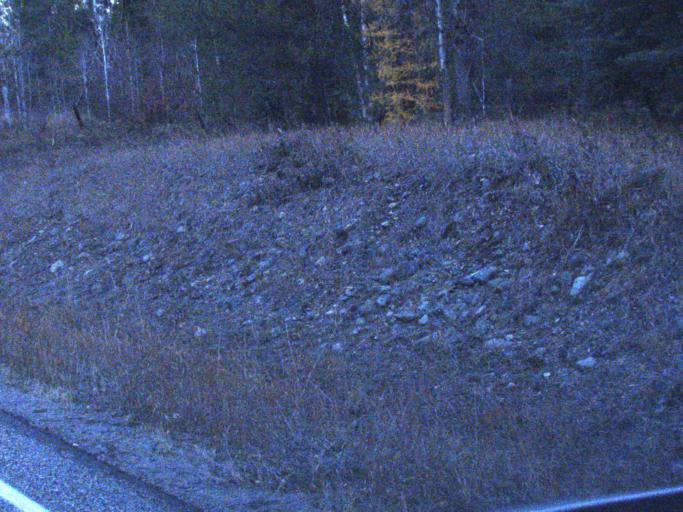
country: CA
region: British Columbia
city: Rossland
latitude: 48.9823
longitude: -117.8259
